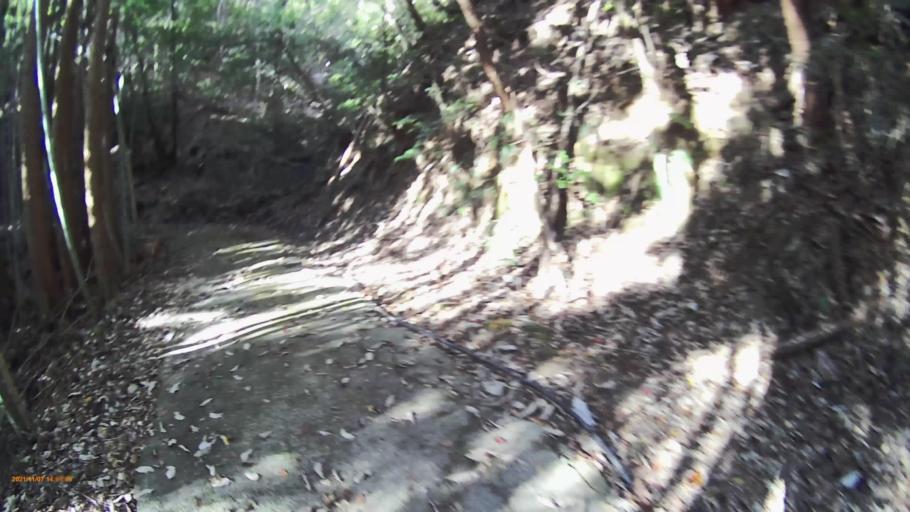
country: JP
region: Gifu
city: Mitake
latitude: 35.4256
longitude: 137.1869
